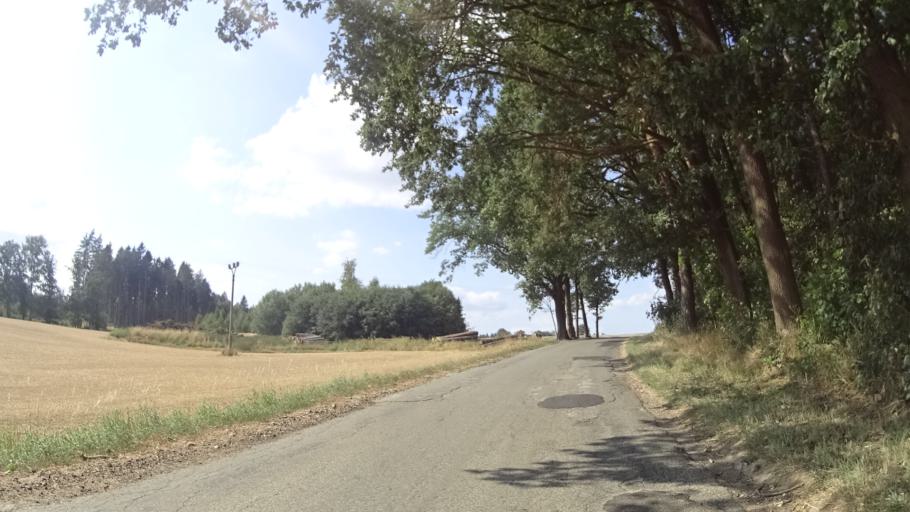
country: CZ
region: Kralovehradecky
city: Liban
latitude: 50.4282
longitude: 15.2581
